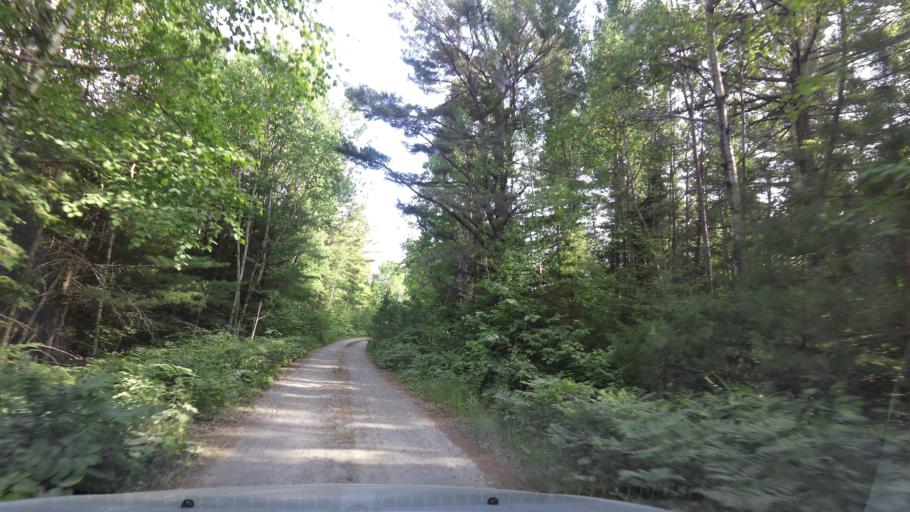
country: CA
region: Ontario
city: Greater Sudbury
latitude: 45.9121
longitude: -80.5541
